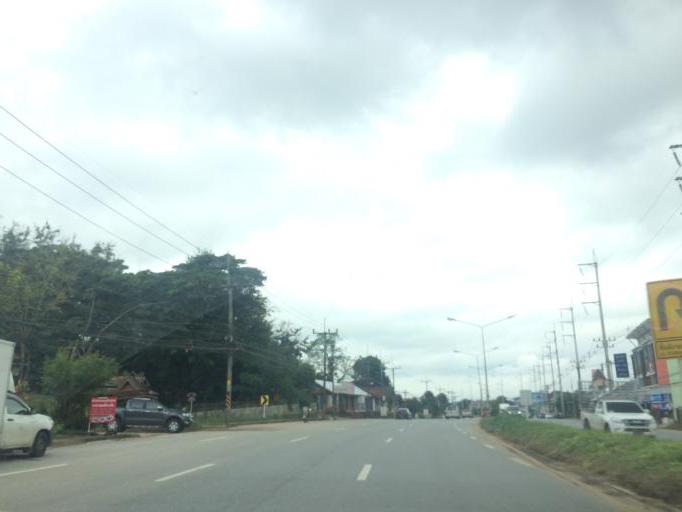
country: TH
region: Chiang Rai
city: Mae Chan
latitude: 20.1317
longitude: 99.8626
